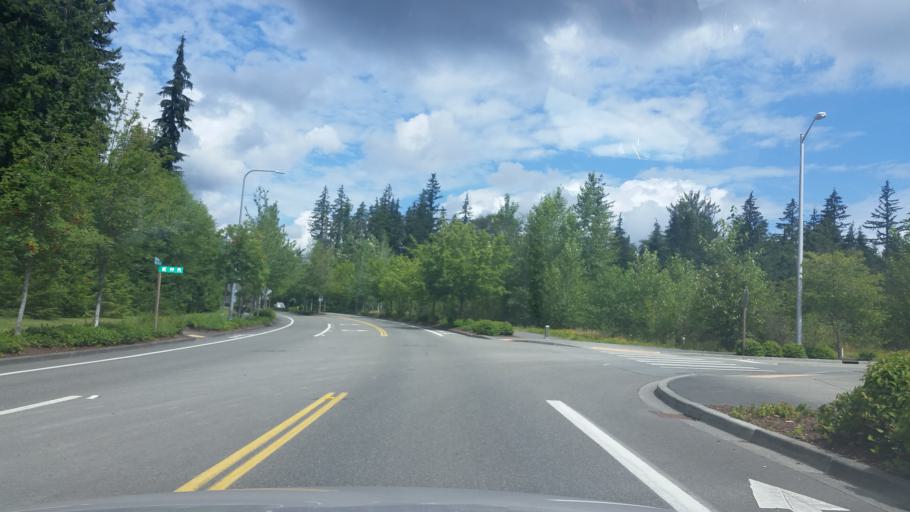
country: US
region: Washington
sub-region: King County
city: Union Hill-Novelty Hill
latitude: 47.6869
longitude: -122.0326
